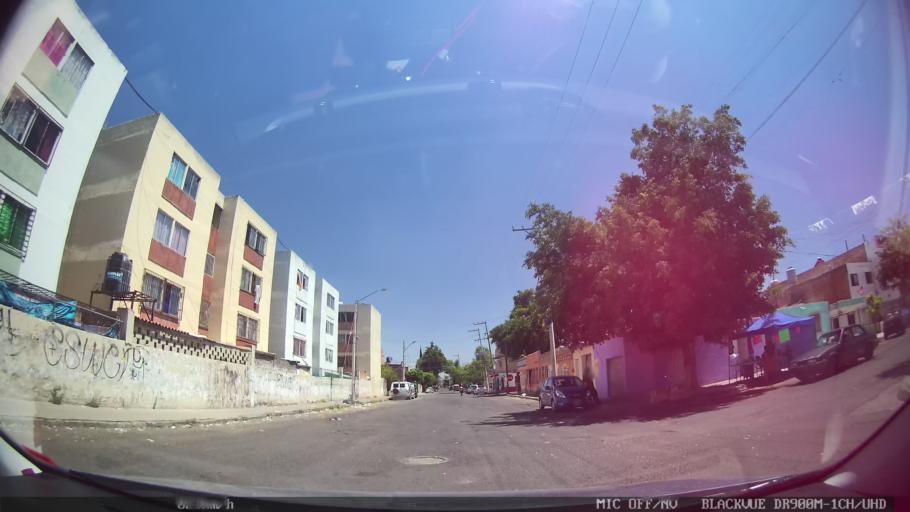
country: MX
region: Jalisco
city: Tlaquepaque
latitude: 20.6649
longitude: -103.2751
